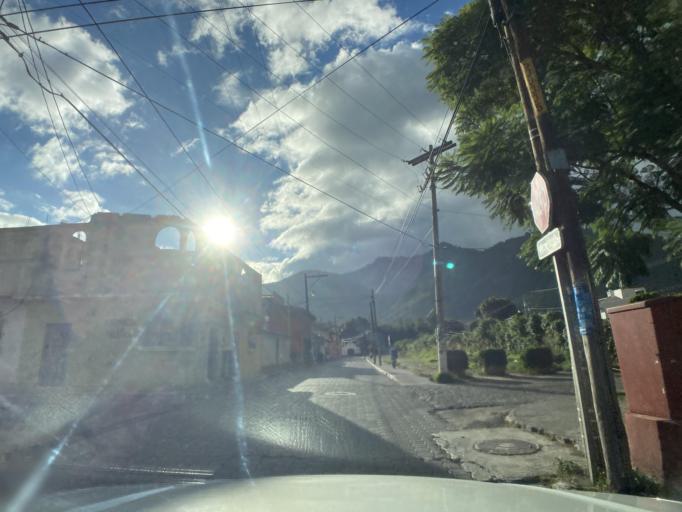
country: GT
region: Sacatepequez
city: Jocotenango
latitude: 14.5746
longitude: -90.7432
